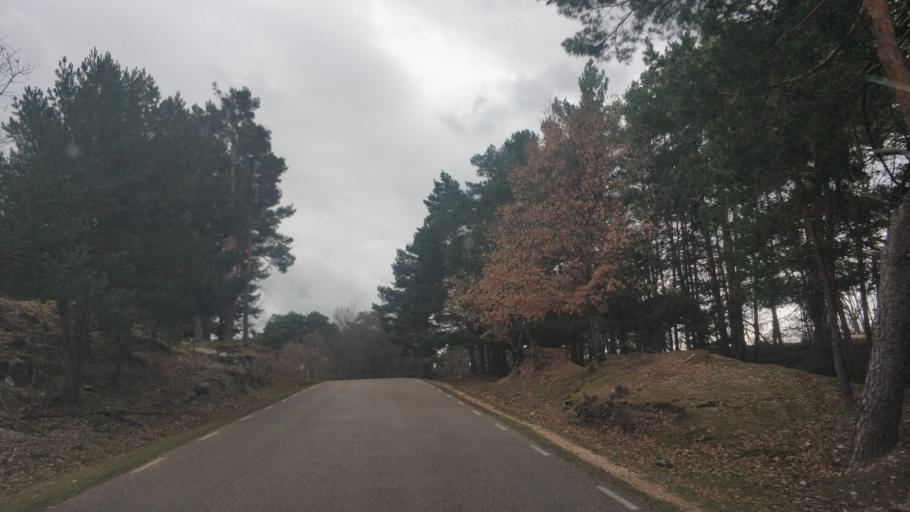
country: ES
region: Castille and Leon
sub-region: Provincia de Burgos
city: Canicosa de la Sierra
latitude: 41.9277
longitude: -3.0410
